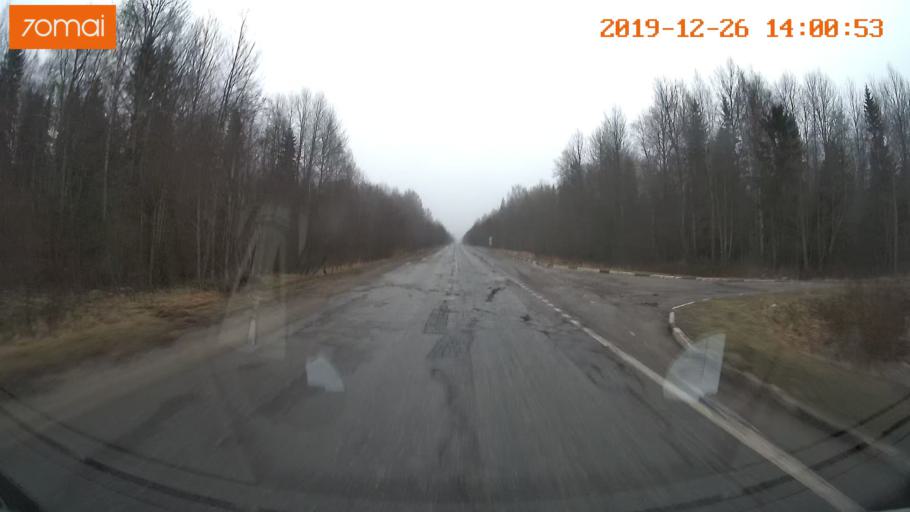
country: RU
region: Jaroslavl
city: Poshekhon'ye
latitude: 58.5547
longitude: 38.7525
